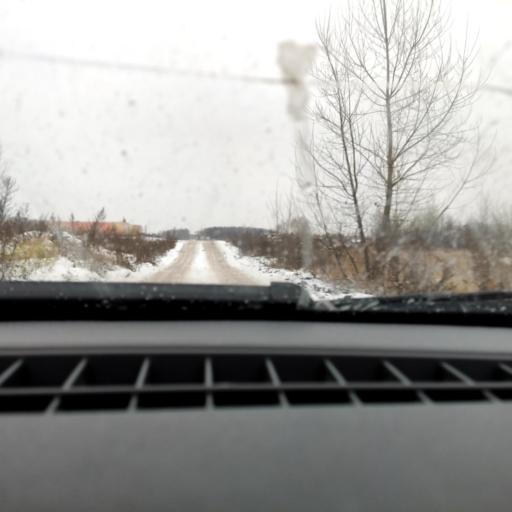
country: RU
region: Bashkortostan
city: Ufa
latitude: 54.6799
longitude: 55.9256
